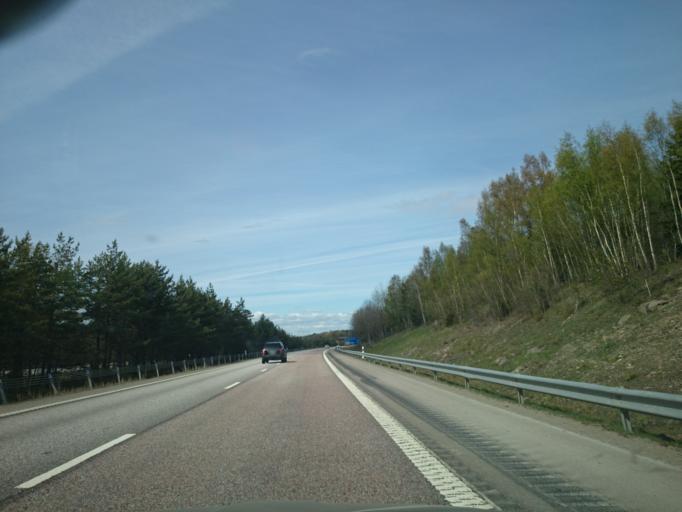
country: SE
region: Uppsala
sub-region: Knivsta Kommun
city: Knivsta
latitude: 59.7356
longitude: 17.8240
